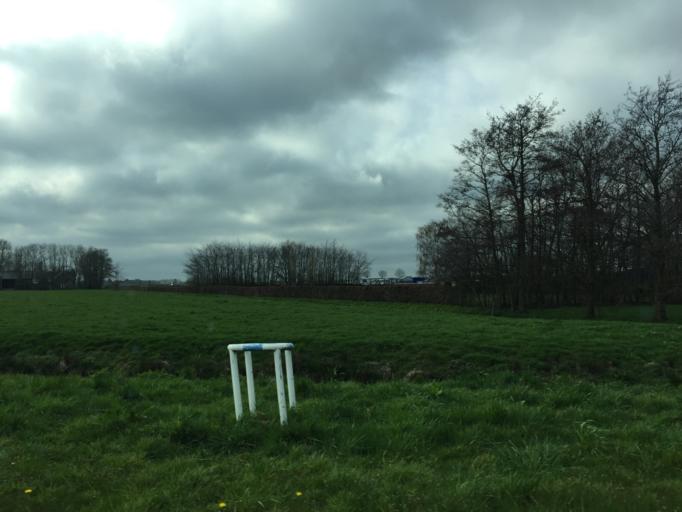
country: NL
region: South Holland
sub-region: Gemeente Kaag en Braassem
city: Oude Wetering
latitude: 52.1973
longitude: 4.6104
